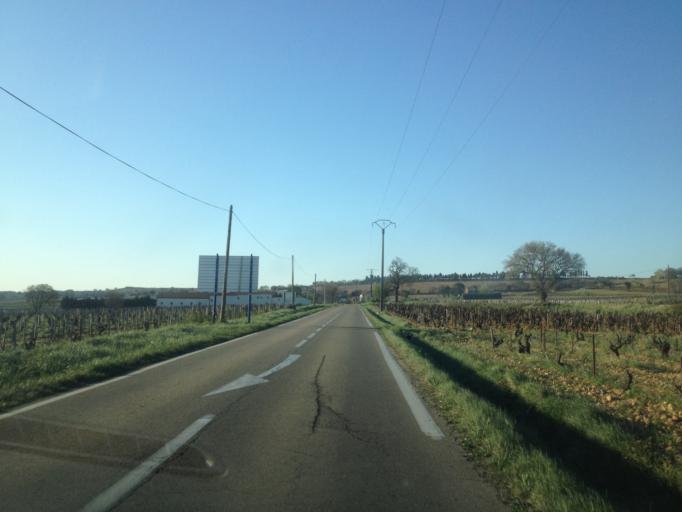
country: FR
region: Provence-Alpes-Cote d'Azur
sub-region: Departement du Vaucluse
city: Chateauneuf-du-Pape
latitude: 44.0947
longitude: 4.8257
